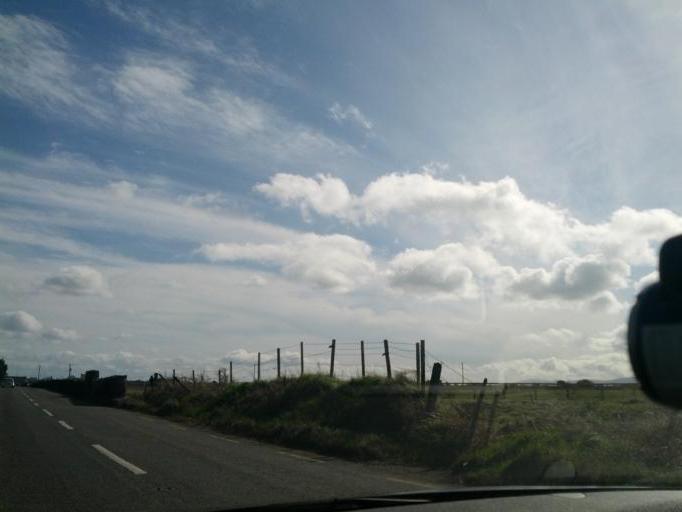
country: IE
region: Leinster
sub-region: Fingal County
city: Baldoyle
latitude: 53.4060
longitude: -6.1341
